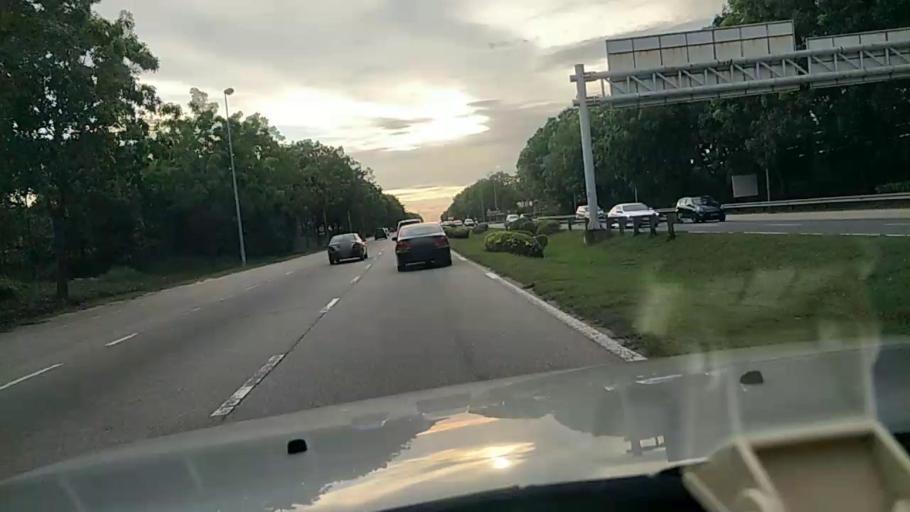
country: MY
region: Selangor
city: Klang
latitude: 3.1081
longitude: 101.4524
